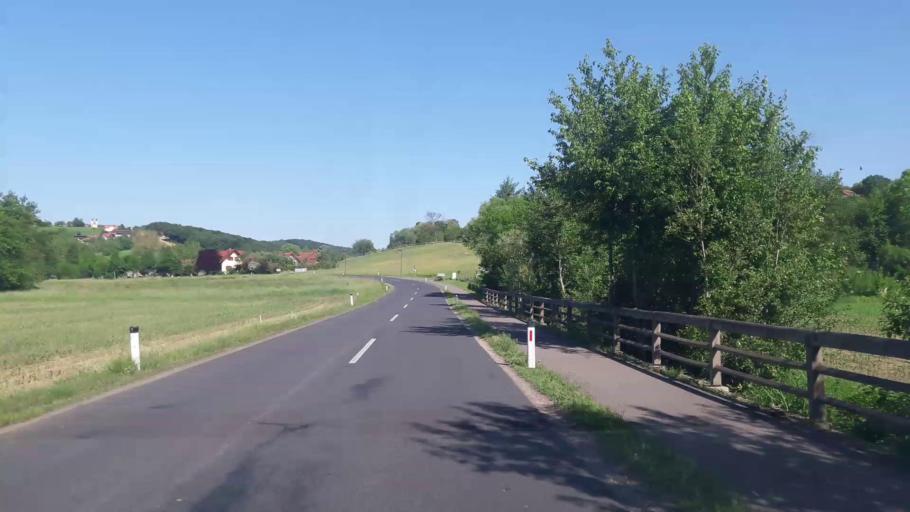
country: AT
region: Styria
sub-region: Politischer Bezirk Suedoststeiermark
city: Unterlamm
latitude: 46.9848
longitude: 16.0531
